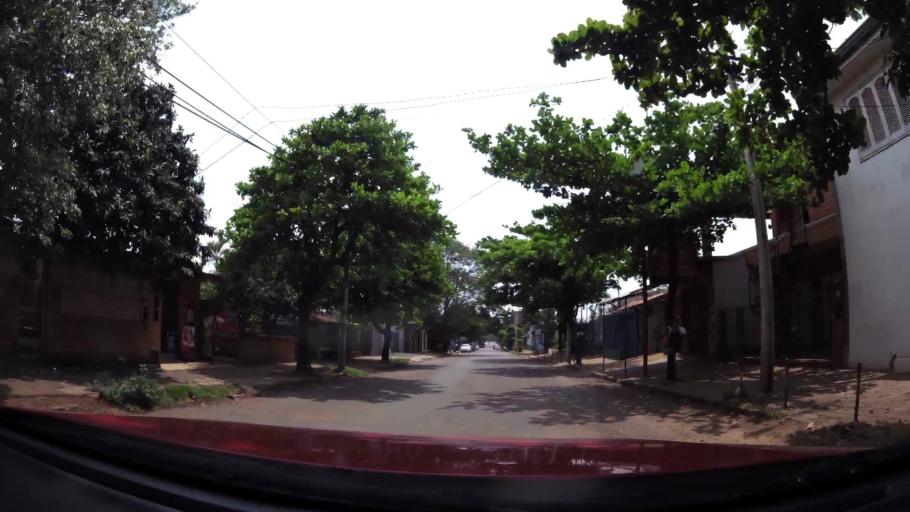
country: PY
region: Central
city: Fernando de la Mora
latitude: -25.3171
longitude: -57.5610
